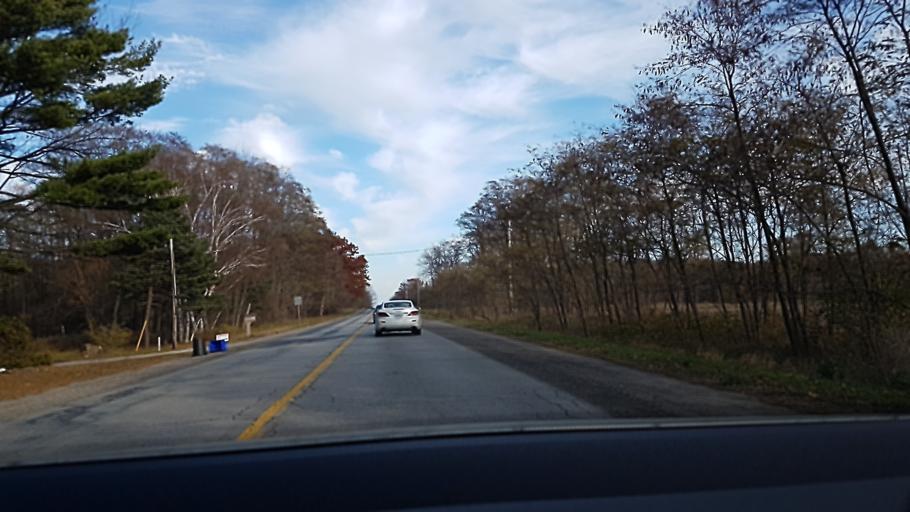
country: CA
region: Ontario
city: Barrie
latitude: 44.3670
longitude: -79.6034
